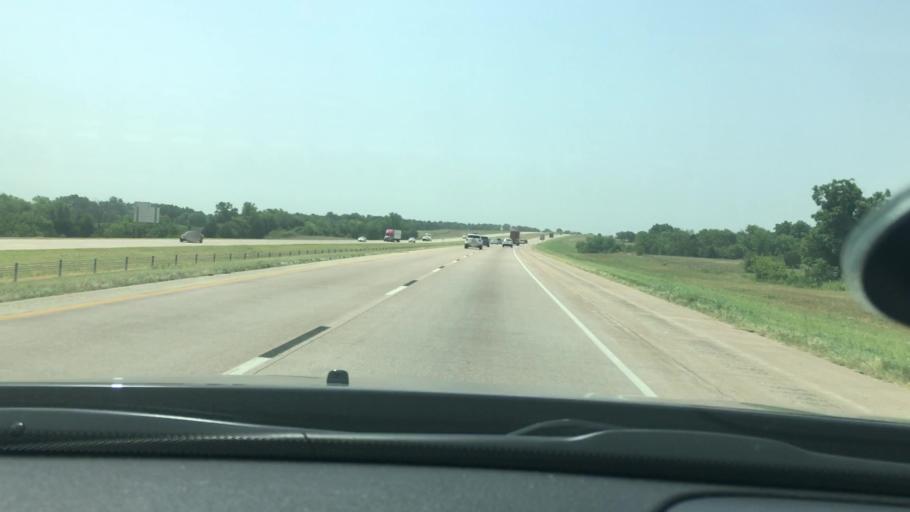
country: US
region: Oklahoma
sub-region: Garvin County
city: Pauls Valley
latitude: 34.6917
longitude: -97.2335
